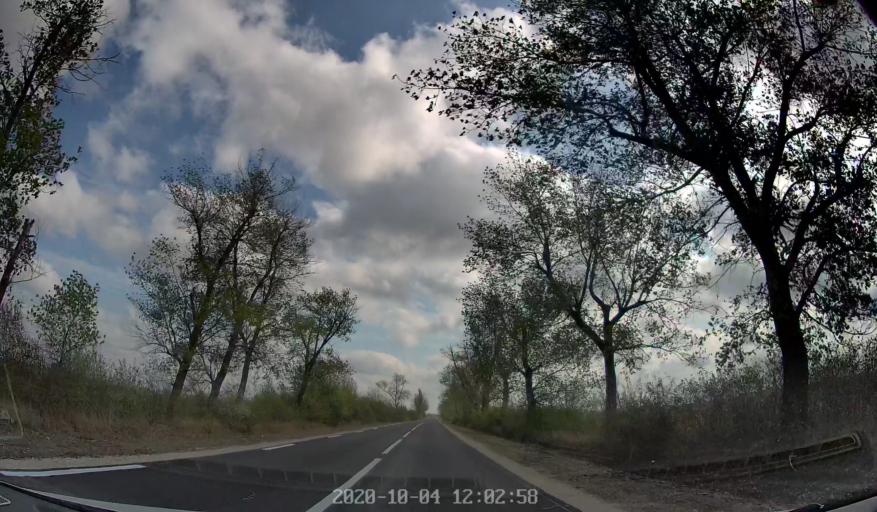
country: MD
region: Rezina
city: Saharna
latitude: 47.6145
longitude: 28.9176
